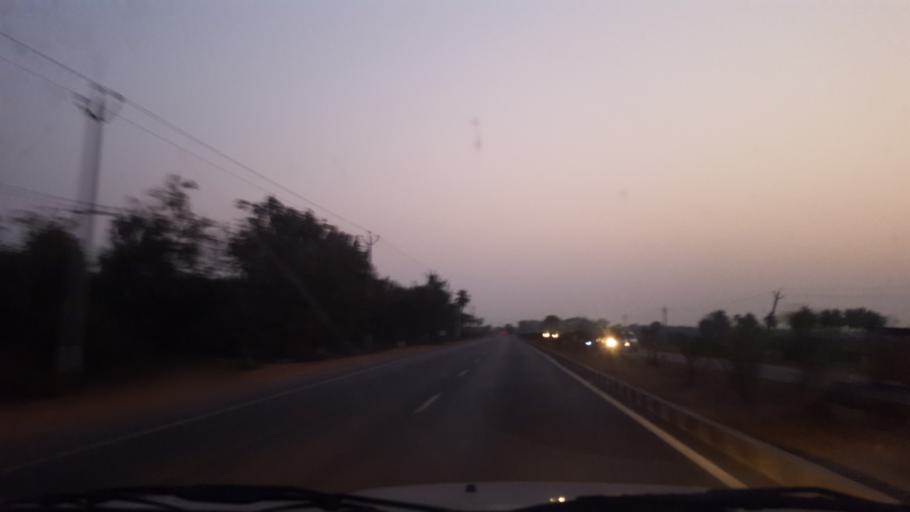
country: IN
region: Andhra Pradesh
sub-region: East Godavari
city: Peddapuram
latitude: 17.1443
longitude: 81.9780
